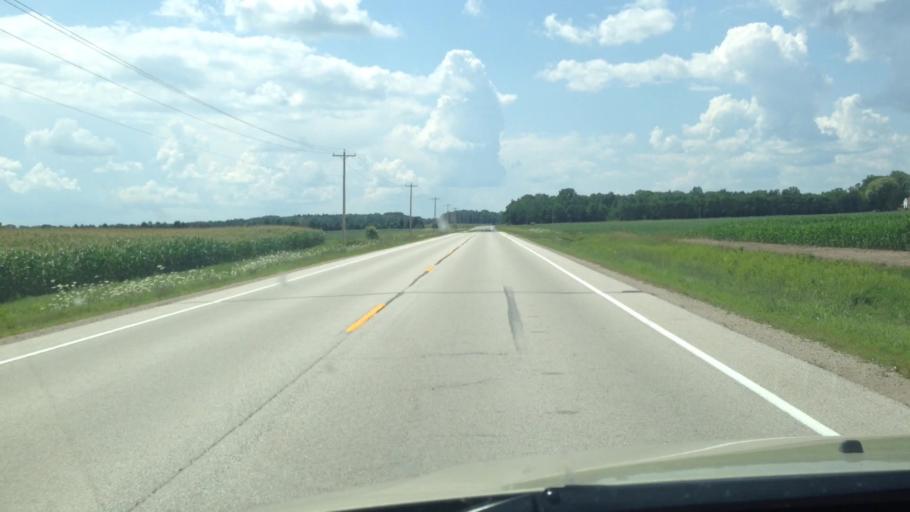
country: US
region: Wisconsin
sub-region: Brown County
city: Pulaski
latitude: 44.6457
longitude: -88.1639
